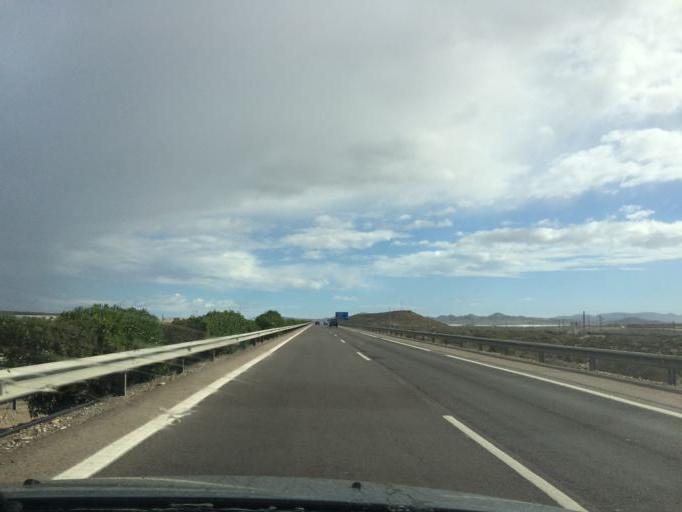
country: ES
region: Andalusia
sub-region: Provincia de Almeria
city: Retamar
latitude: 36.8639
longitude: -2.2486
